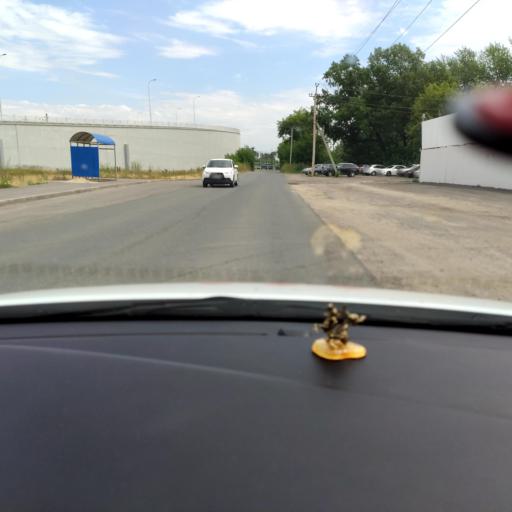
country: RU
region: Tatarstan
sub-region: Zelenodol'skiy Rayon
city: Zelenodolsk
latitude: 55.8402
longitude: 48.5417
